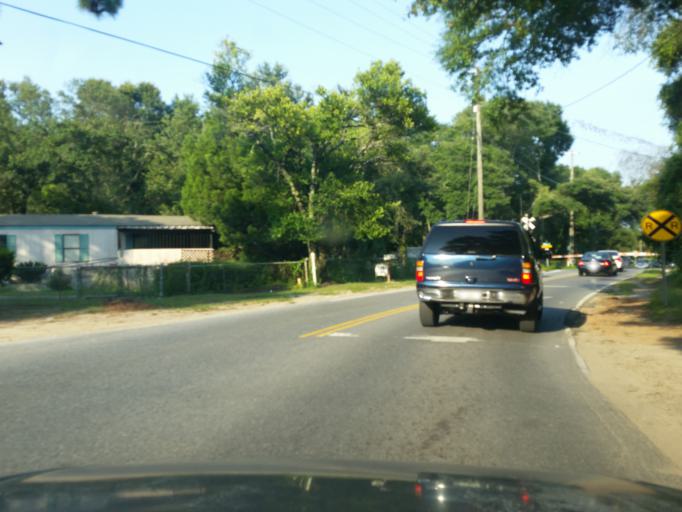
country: US
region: Florida
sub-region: Escambia County
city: Ensley
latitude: 30.4986
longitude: -87.2682
